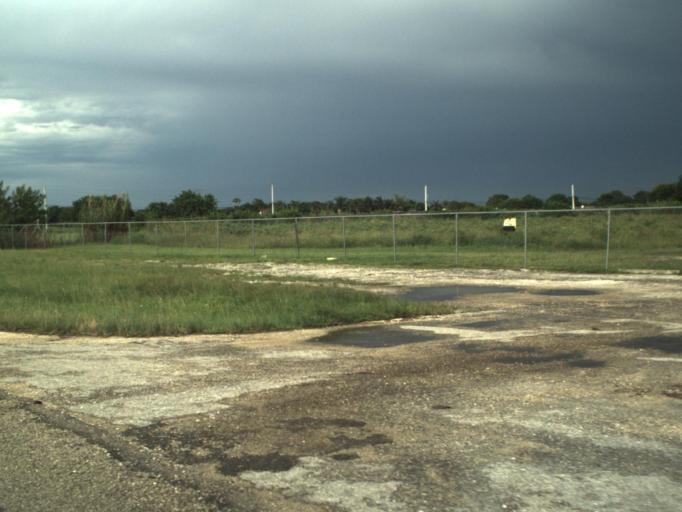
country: US
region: Florida
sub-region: Miami-Dade County
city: Richmond West
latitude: 25.5777
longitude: -80.4783
